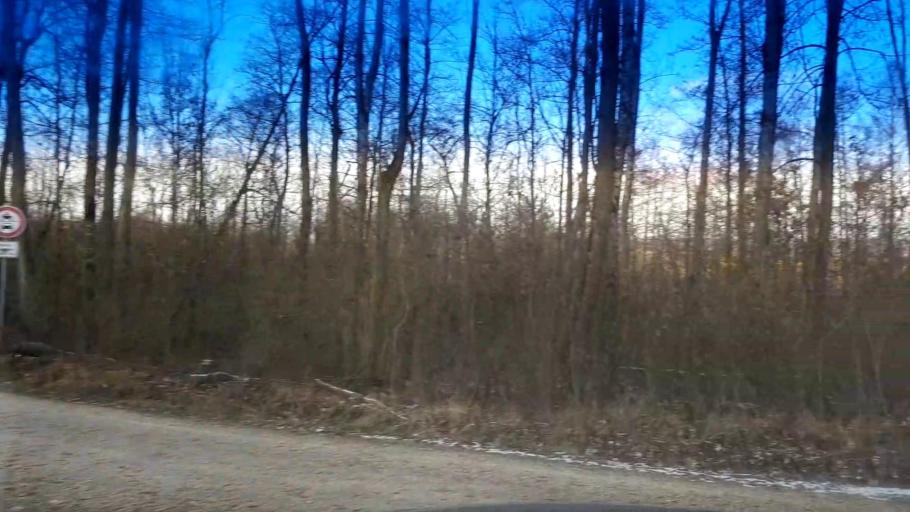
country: DE
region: Bavaria
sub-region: Upper Franconia
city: Schesslitz
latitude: 49.9875
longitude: 11.0049
